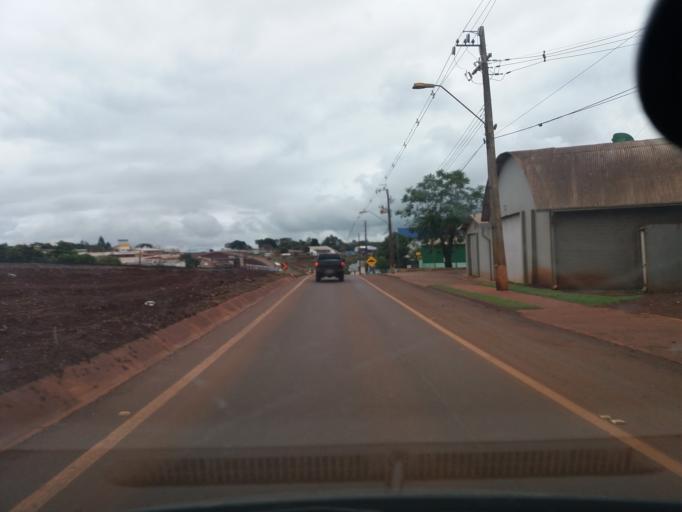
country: BR
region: Parana
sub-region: Corbelia
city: Corbelia
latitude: -24.7979
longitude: -53.2890
